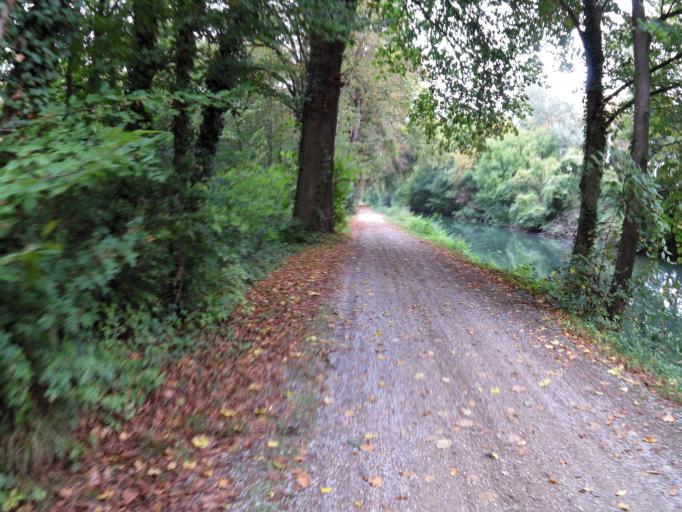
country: FR
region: Alsace
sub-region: Departement du Bas-Rhin
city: Marckolsheim
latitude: 48.1414
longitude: 7.5342
